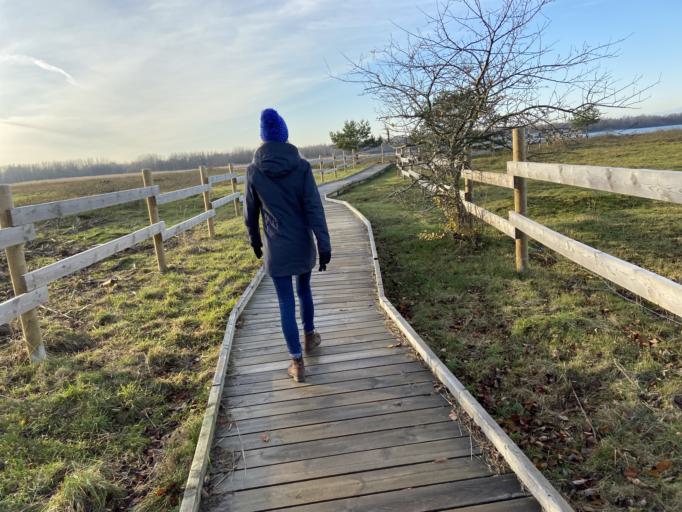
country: EE
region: Harju
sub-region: Tallinna linn
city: Tallinn
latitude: 59.4826
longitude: 24.7089
